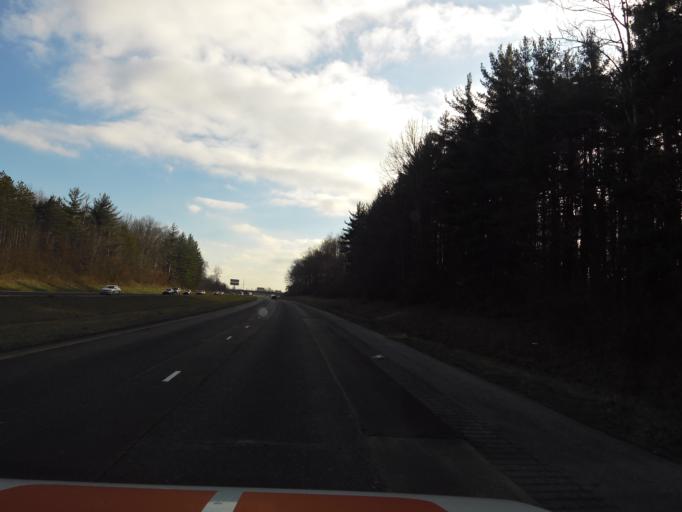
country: US
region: Indiana
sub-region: Scott County
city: Scottsburg
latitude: 38.6765
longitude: -85.7865
